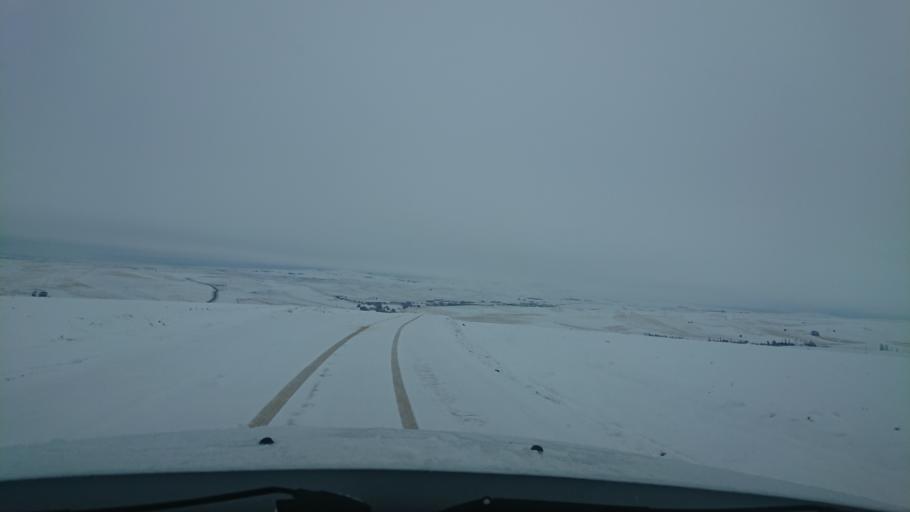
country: TR
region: Aksaray
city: Agacoren
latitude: 38.7478
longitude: 33.8746
